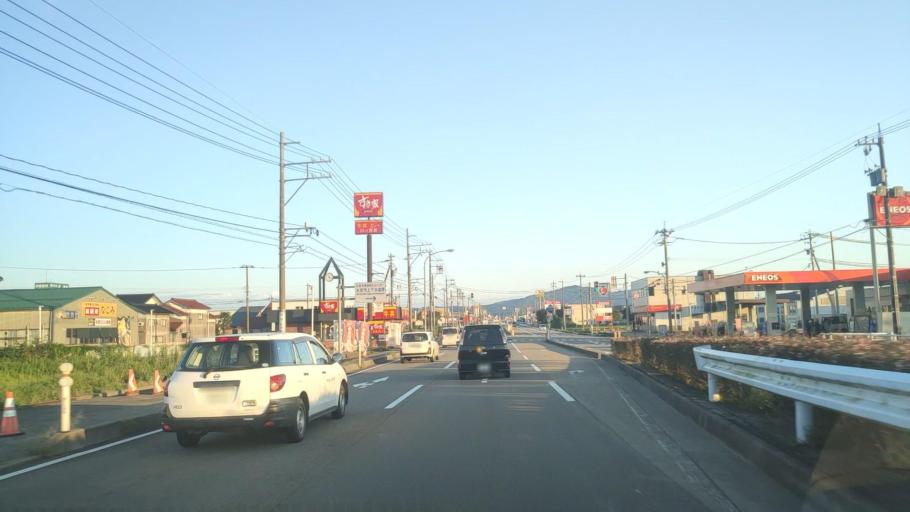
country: JP
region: Toyama
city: Himi
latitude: 36.8424
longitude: 136.9836
